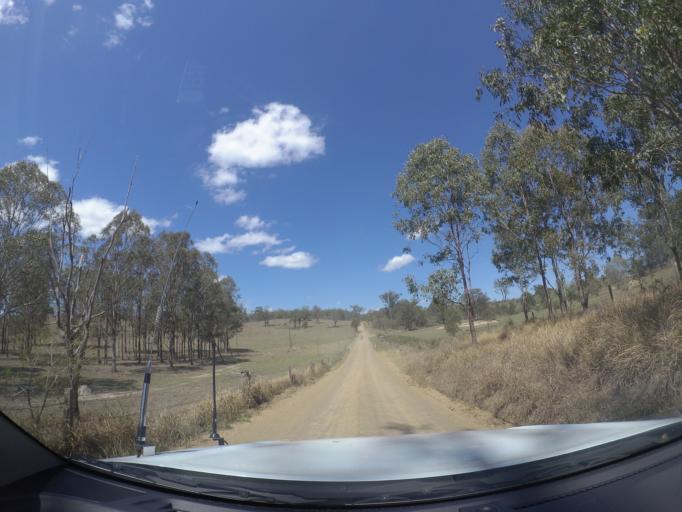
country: AU
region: Queensland
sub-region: Logan
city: Cedar Vale
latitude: -27.8520
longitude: 152.8871
